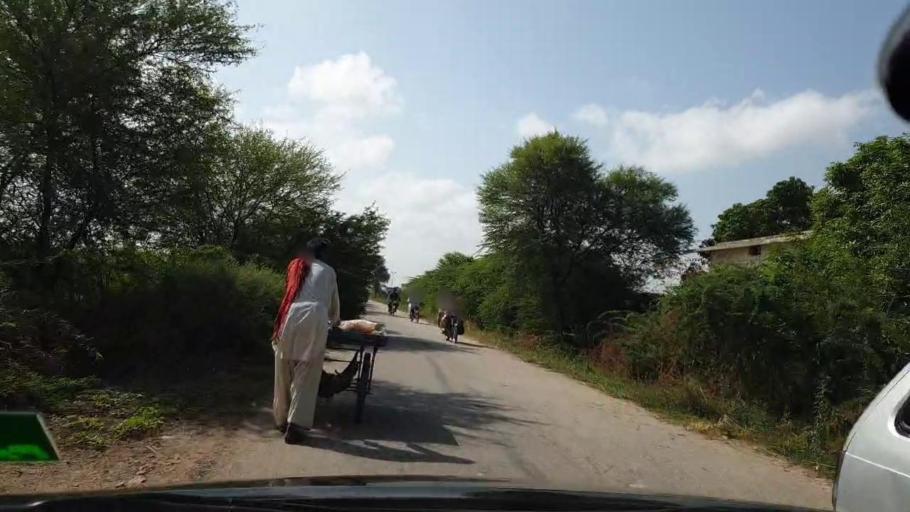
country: PK
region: Sindh
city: Kadhan
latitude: 24.6344
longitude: 69.1159
